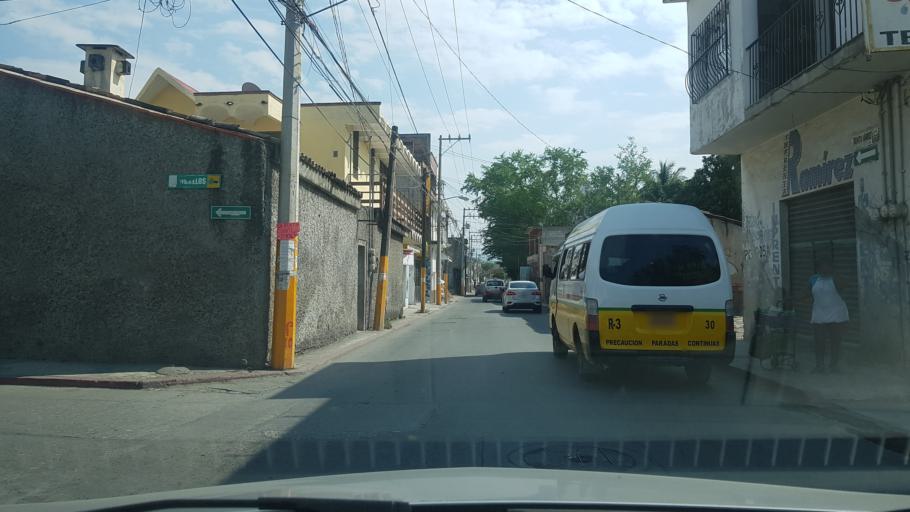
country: MX
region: Morelos
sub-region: Jojutla
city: Jojutla
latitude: 18.6183
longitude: -99.1821
